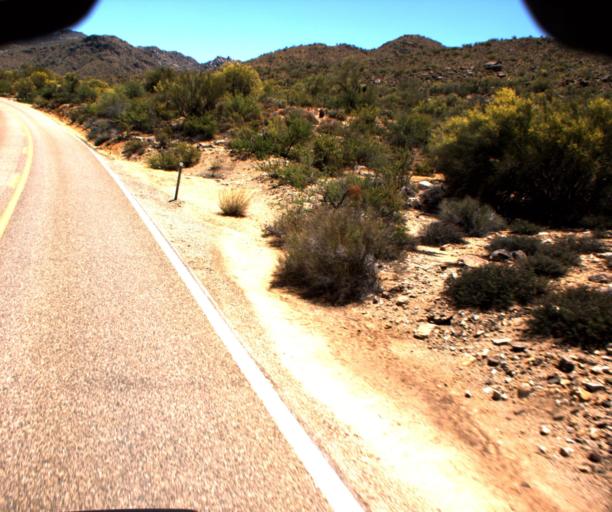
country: US
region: Arizona
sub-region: Yavapai County
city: Bagdad
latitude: 34.4609
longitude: -113.0398
